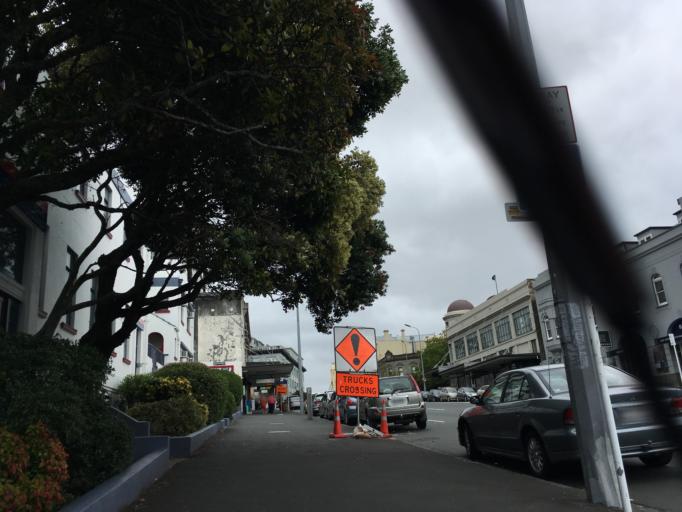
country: NZ
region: Auckland
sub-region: Auckland
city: Auckland
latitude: -36.8562
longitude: 174.7590
